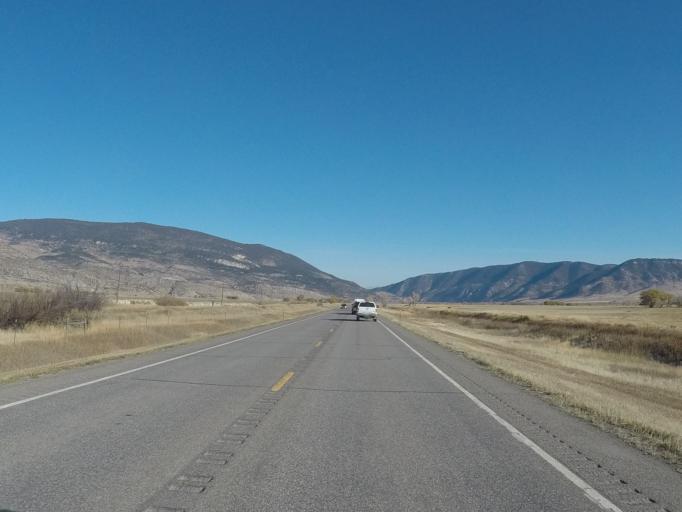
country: US
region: Montana
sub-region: Park County
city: Livingston
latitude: 45.5324
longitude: -110.6046
